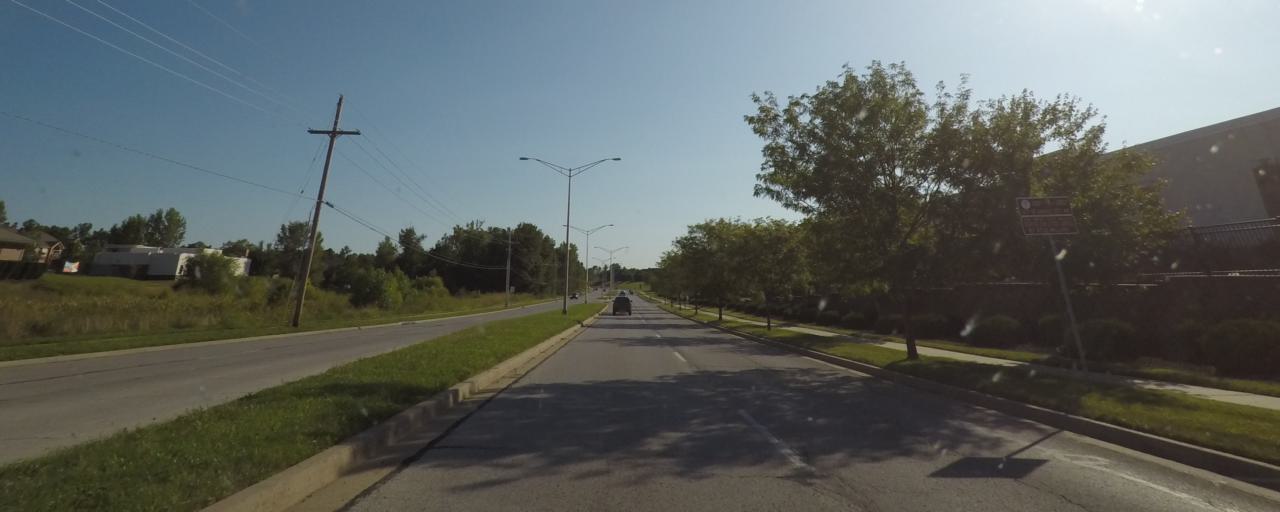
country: US
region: Missouri
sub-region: Clay County
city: Pleasant Valley
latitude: 39.2404
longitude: -94.4665
